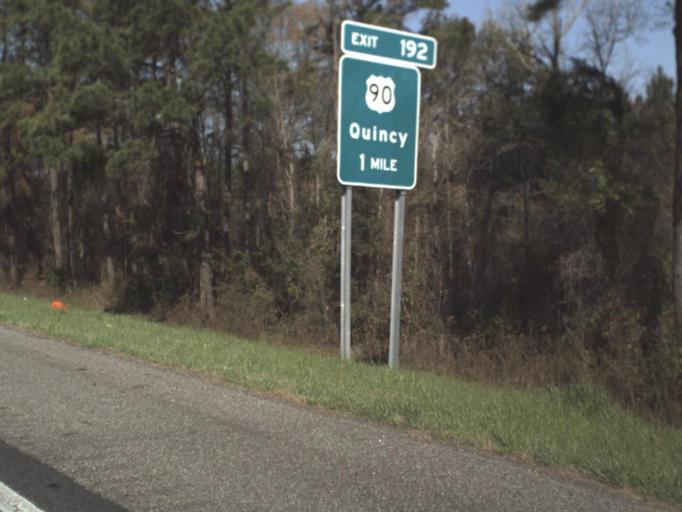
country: US
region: Florida
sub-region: Gadsden County
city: Midway
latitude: 30.4857
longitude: -84.4044
